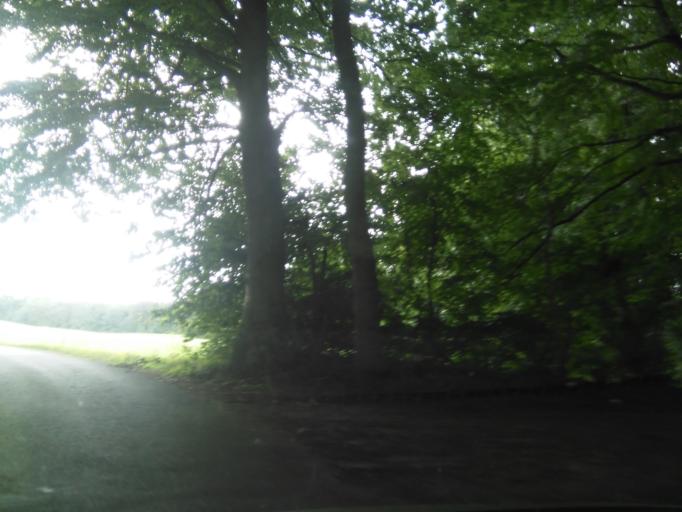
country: DK
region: Central Jutland
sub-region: Odder Kommune
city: Odder
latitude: 55.9379
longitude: 10.1040
